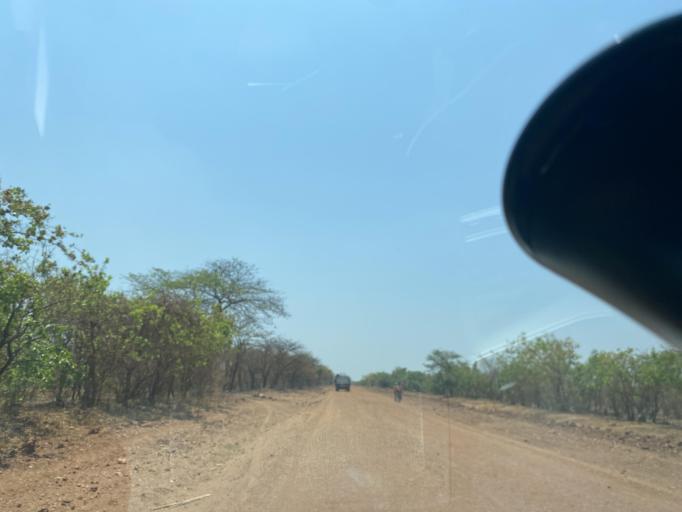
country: ZM
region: Lusaka
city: Lusaka
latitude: -15.4579
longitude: 27.9341
